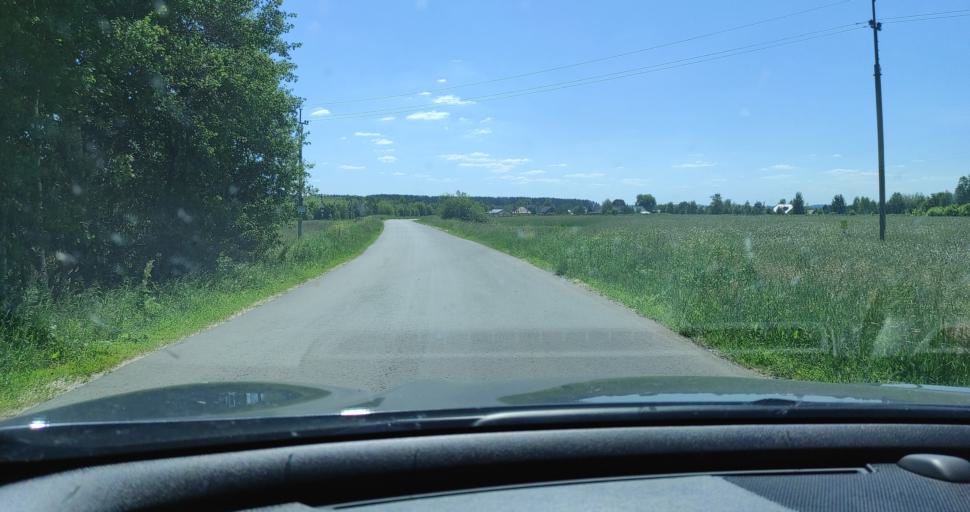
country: RU
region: Rjazan
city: Murmino
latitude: 54.5688
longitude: 40.0957
